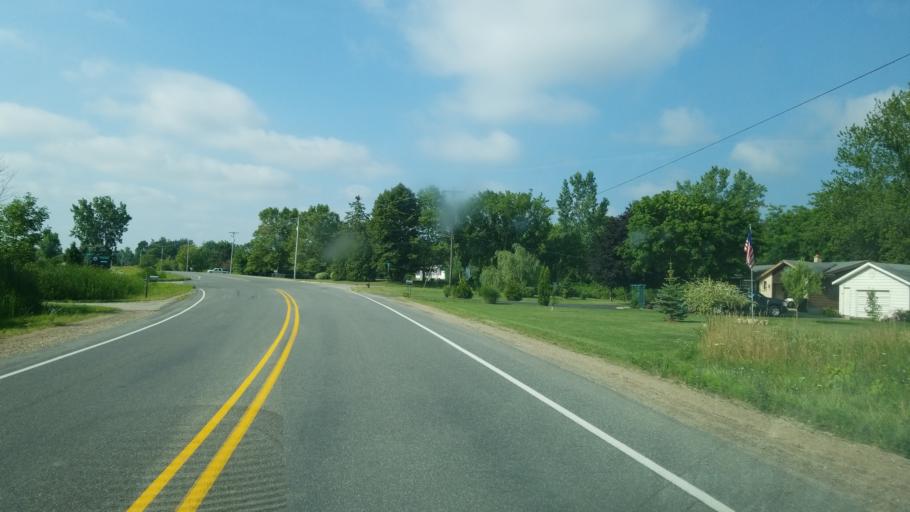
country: US
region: Michigan
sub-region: Kent County
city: Comstock Park
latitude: 43.0805
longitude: -85.6536
